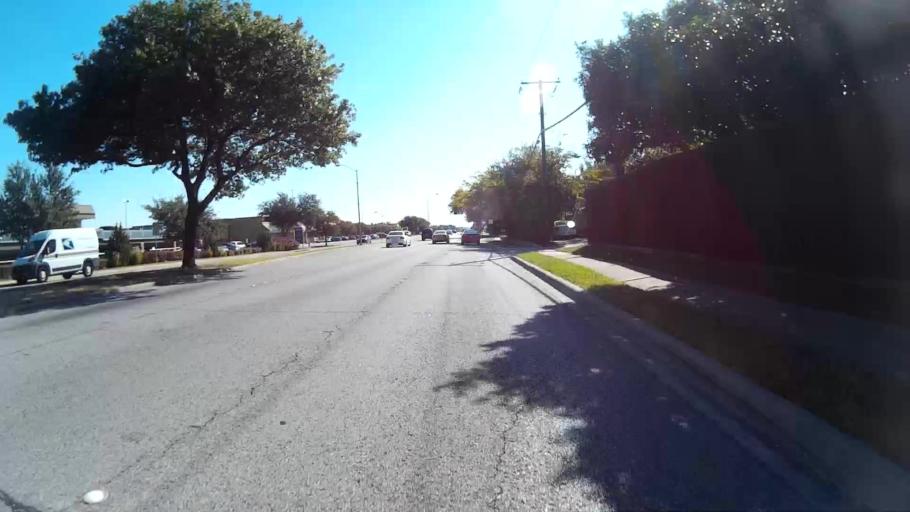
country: US
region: Texas
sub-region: Dallas County
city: Richardson
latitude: 32.9547
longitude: -96.7690
